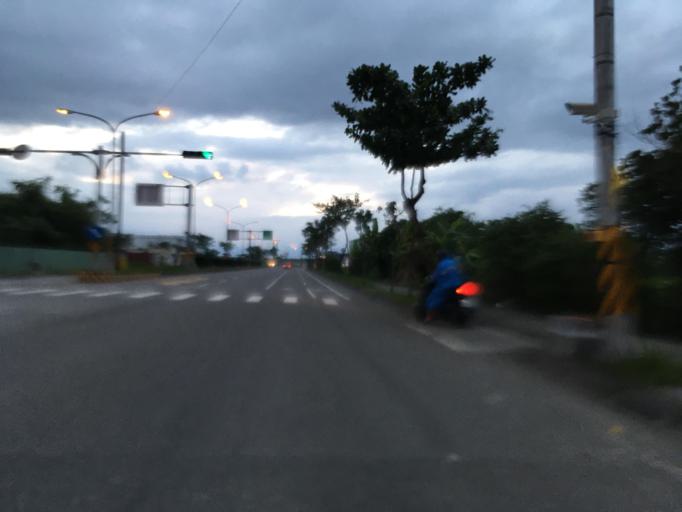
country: TW
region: Taiwan
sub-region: Yilan
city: Yilan
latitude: 24.6260
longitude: 121.8347
